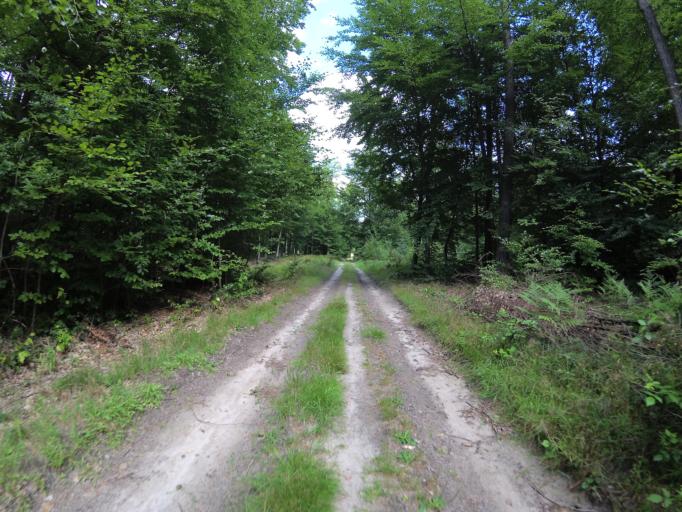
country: PL
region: Pomeranian Voivodeship
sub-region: Gdynia
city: Wielki Kack
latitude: 54.5104
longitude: 18.4778
